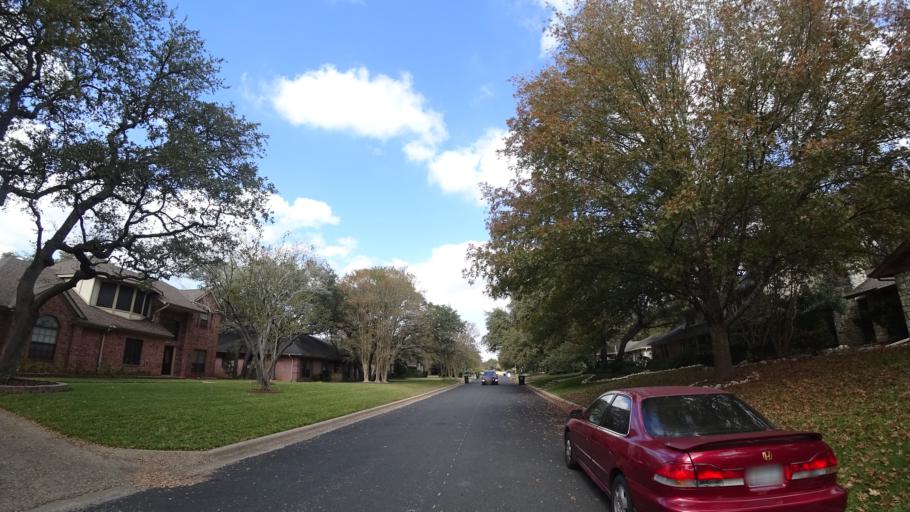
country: US
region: Texas
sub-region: Travis County
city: Shady Hollow
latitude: 30.1712
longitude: -97.8522
